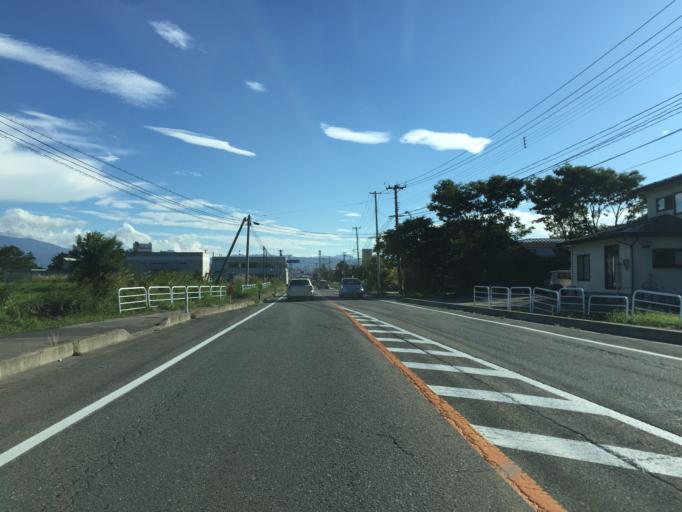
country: JP
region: Yamagata
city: Yonezawa
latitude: 37.9699
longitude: 140.1311
